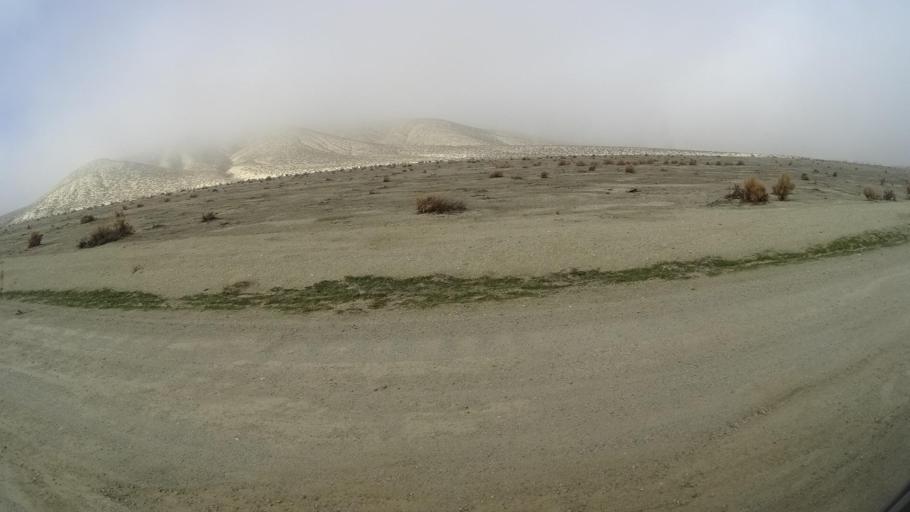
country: US
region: California
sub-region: Kern County
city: Maricopa
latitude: 35.0376
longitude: -119.4328
